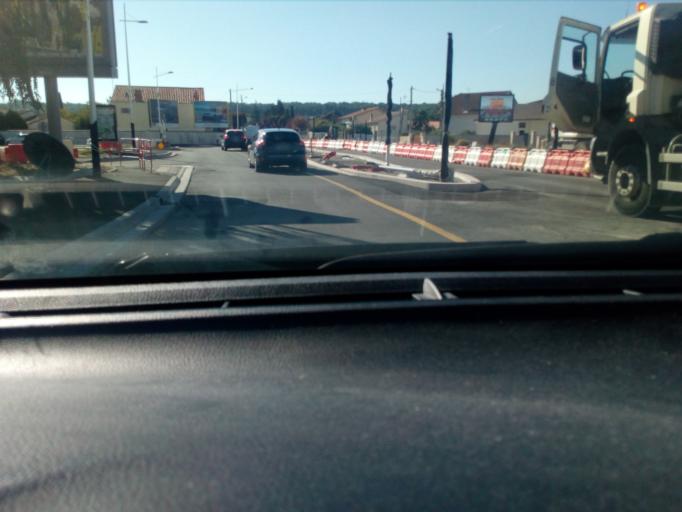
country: FR
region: Poitou-Charentes
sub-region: Departement de la Charente
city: Angouleme
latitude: 45.6462
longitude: 0.1327
